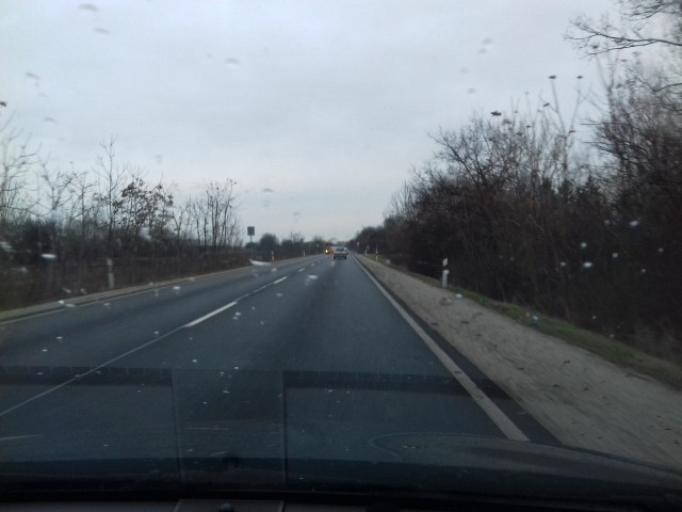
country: HU
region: Szabolcs-Szatmar-Bereg
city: Ujfeherto
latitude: 47.8609
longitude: 21.7045
